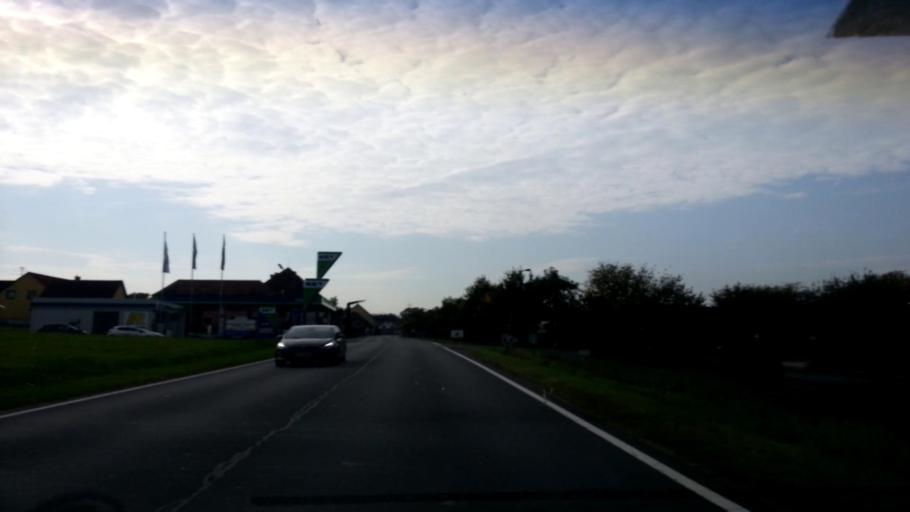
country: DE
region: Bavaria
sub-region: Regierungsbezirk Unterfranken
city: Castell
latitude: 49.7690
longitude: 10.3414
